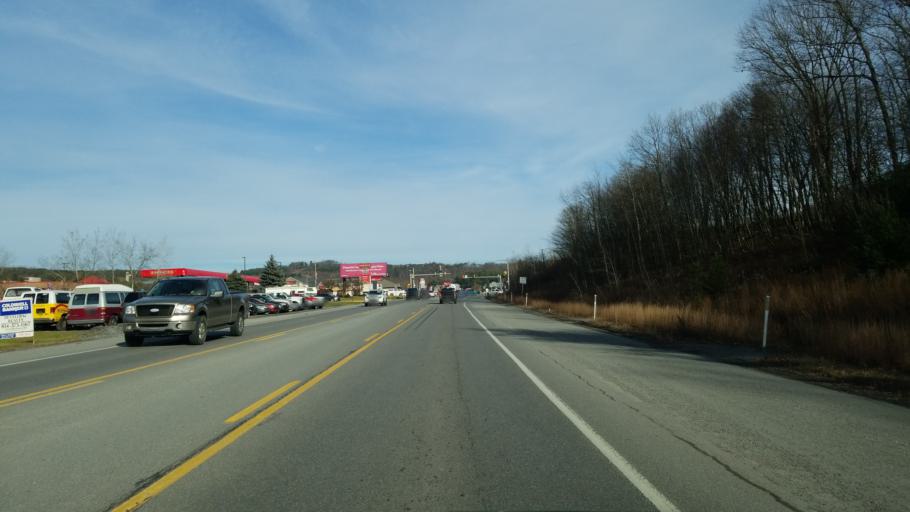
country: US
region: Pennsylvania
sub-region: Clearfield County
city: Clearfield
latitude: 41.0328
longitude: -78.4053
